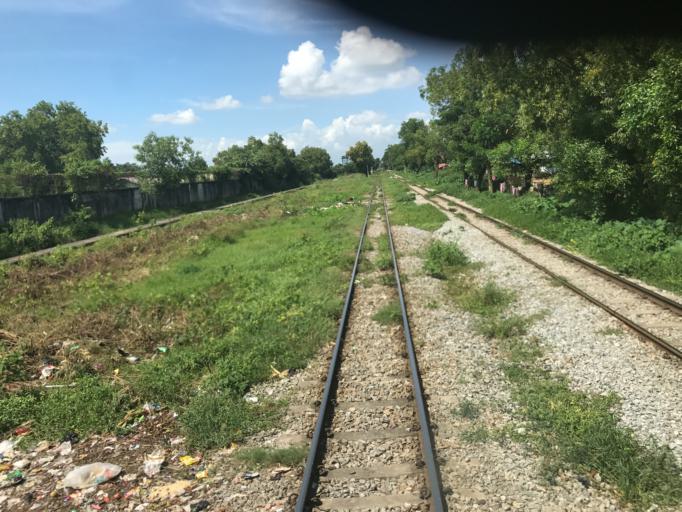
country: MM
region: Yangon
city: Yangon
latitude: 16.9117
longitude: 96.0927
